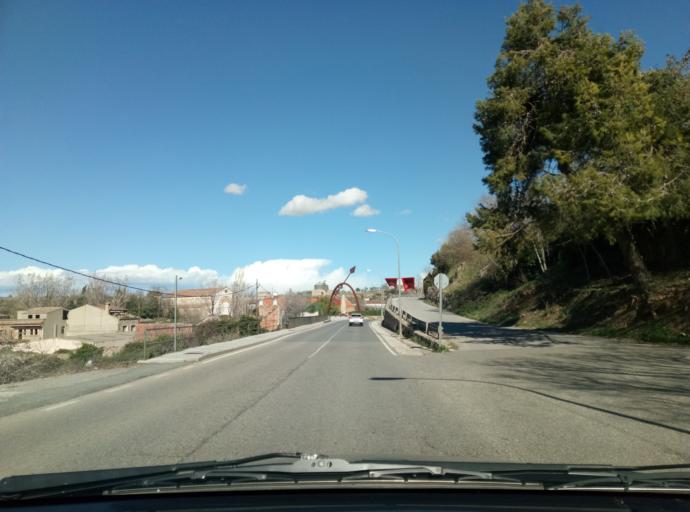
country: ES
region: Catalonia
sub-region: Provincia de Tarragona
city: Vimbodi
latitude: 41.3979
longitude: 1.1013
